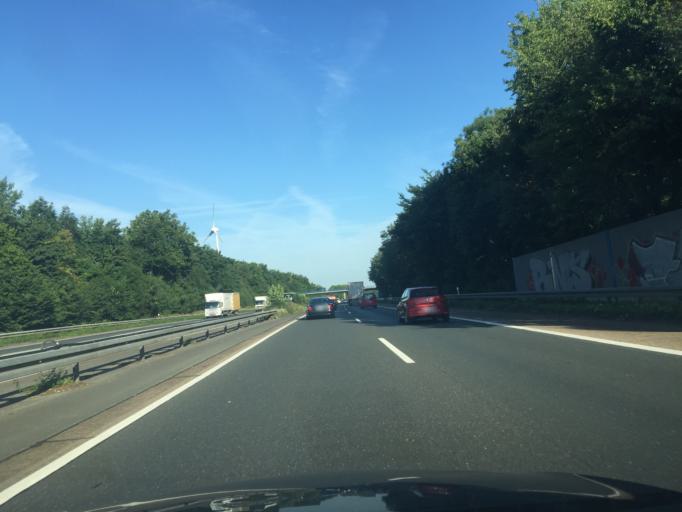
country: DE
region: North Rhine-Westphalia
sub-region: Regierungsbezirk Arnsberg
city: Nachrodt-Wiblingwerde
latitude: 51.3195
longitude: 7.5424
